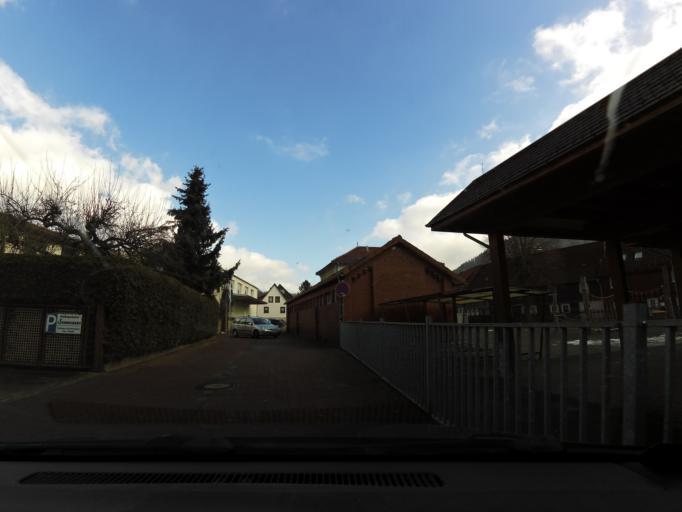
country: DE
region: Lower Saxony
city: Bad Lauterberg im Harz
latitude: 51.6283
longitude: 10.4656
